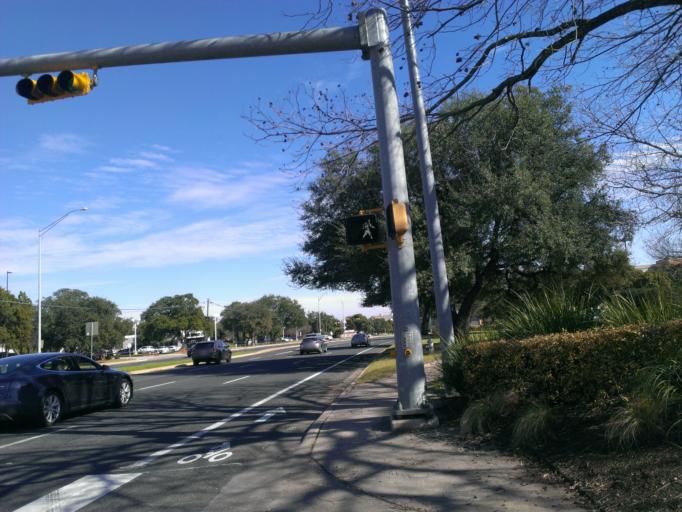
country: US
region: Texas
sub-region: Williamson County
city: Jollyville
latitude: 30.3904
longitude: -97.7415
